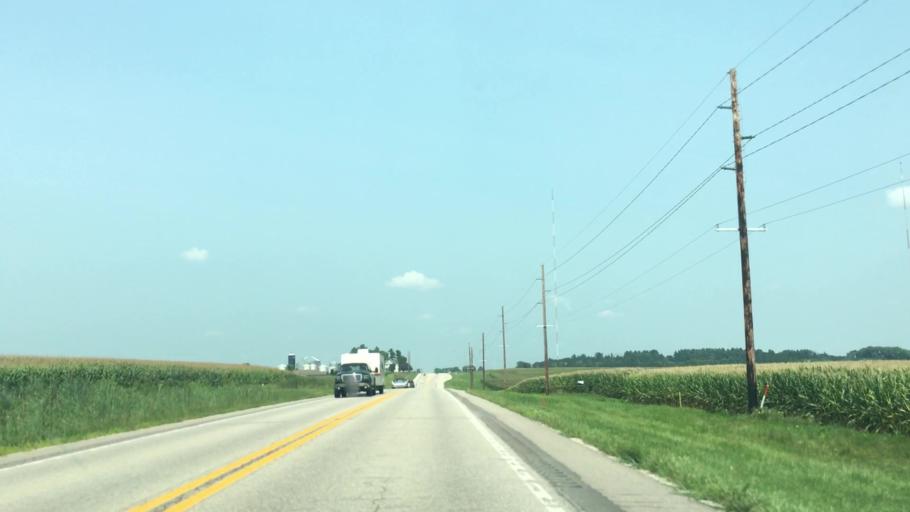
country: US
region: Iowa
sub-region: Benton County
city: Urbana
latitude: 42.2771
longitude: -91.8902
